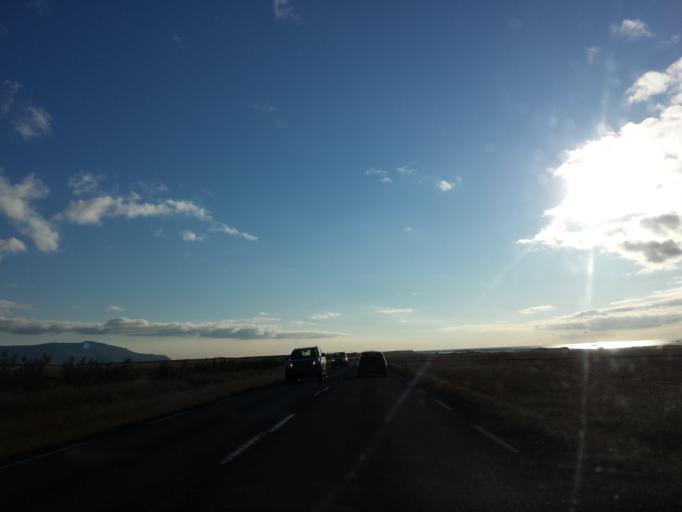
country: IS
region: West
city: Borgarnes
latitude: 64.4834
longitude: -21.9536
